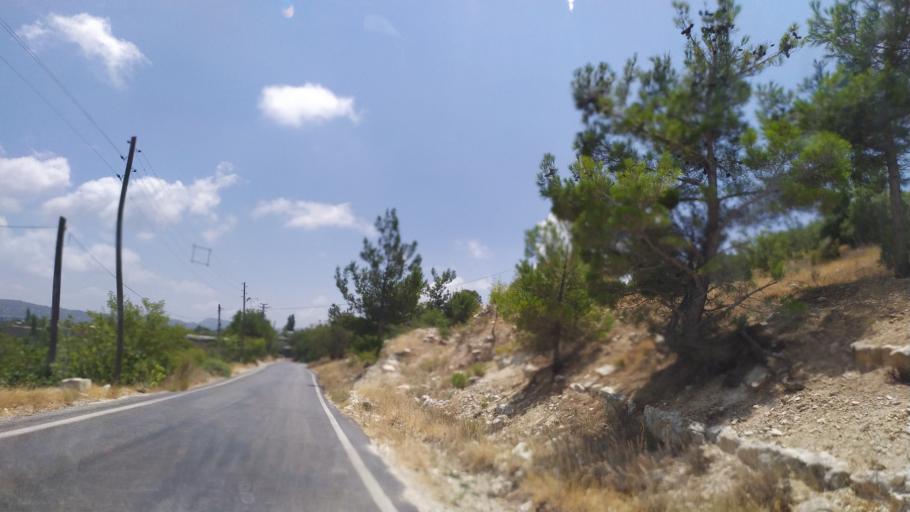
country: TR
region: Mersin
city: Gulnar
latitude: 36.2868
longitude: 33.3830
